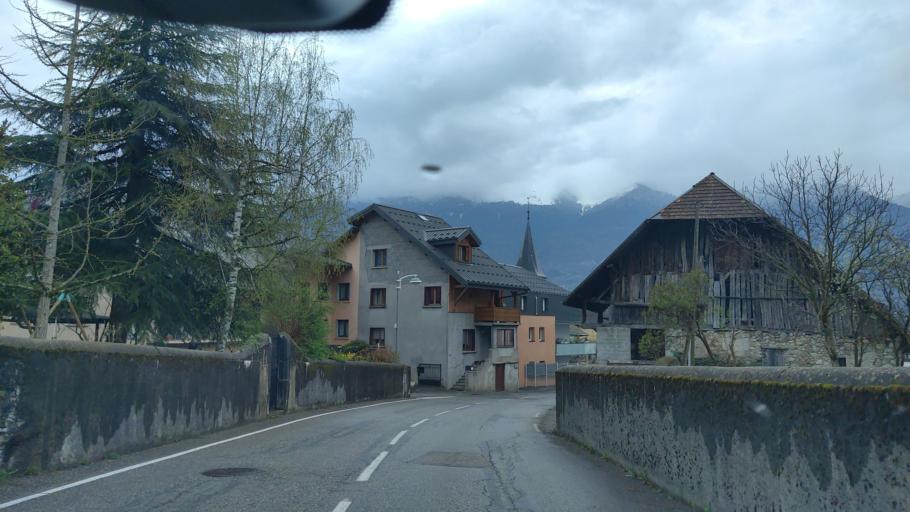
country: FR
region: Rhone-Alpes
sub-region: Departement de la Savoie
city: Frontenex
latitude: 45.6381
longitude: 6.3076
